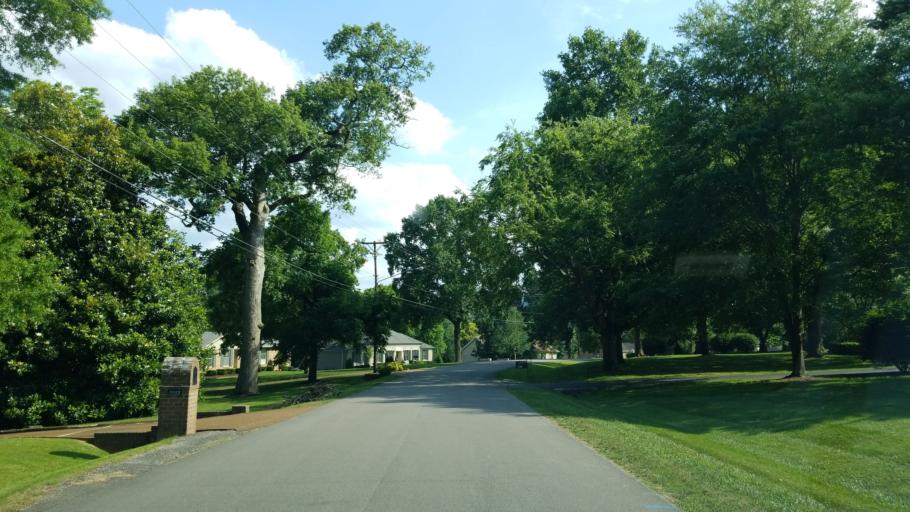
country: US
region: Tennessee
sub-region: Davidson County
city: Forest Hills
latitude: 36.0369
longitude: -86.8284
